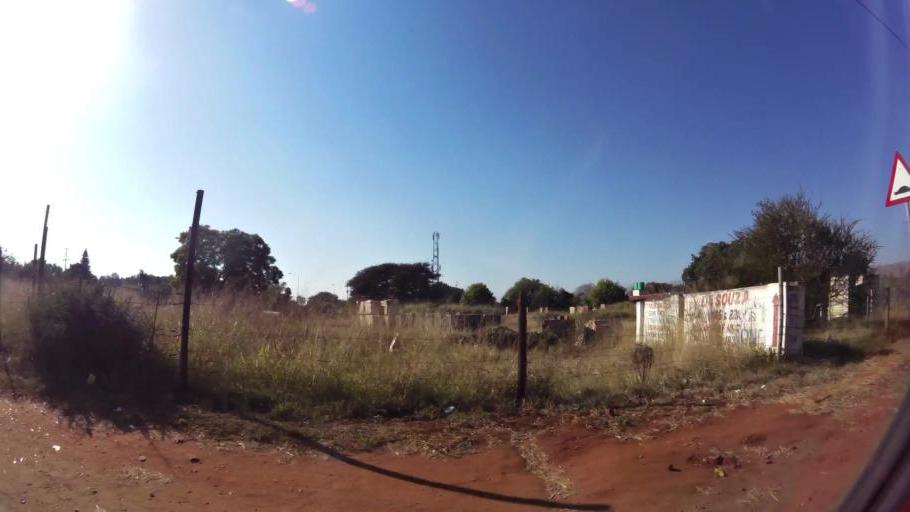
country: ZA
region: Gauteng
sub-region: City of Tshwane Metropolitan Municipality
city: Pretoria
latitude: -25.6556
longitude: 28.1437
